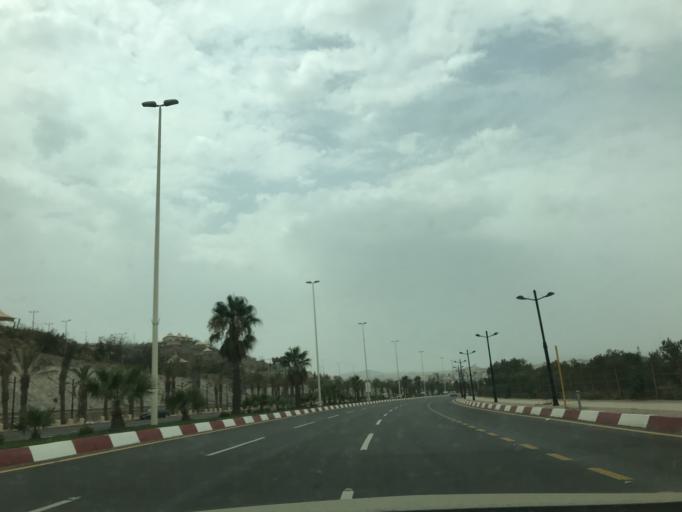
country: SA
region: Mintaqat al Bahah
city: Al Bahah
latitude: 19.8438
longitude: 41.5872
